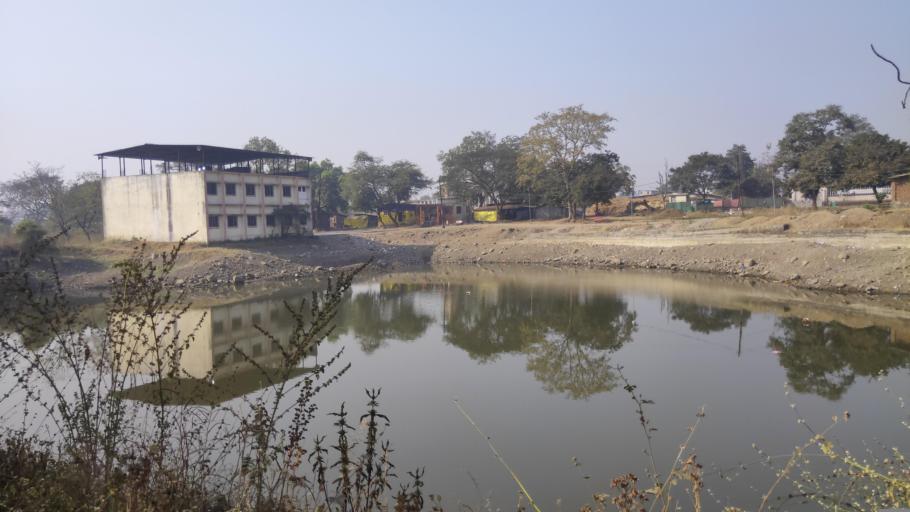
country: IN
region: Maharashtra
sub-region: Thane
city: Bhiwandi
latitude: 19.3163
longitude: 73.0545
